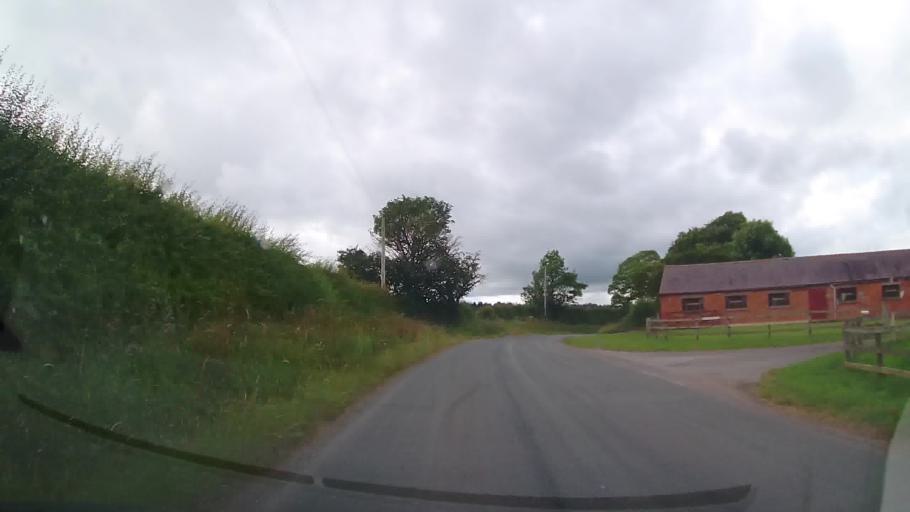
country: GB
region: England
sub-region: Shropshire
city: Whitchurch
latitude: 52.9281
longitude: -2.7309
